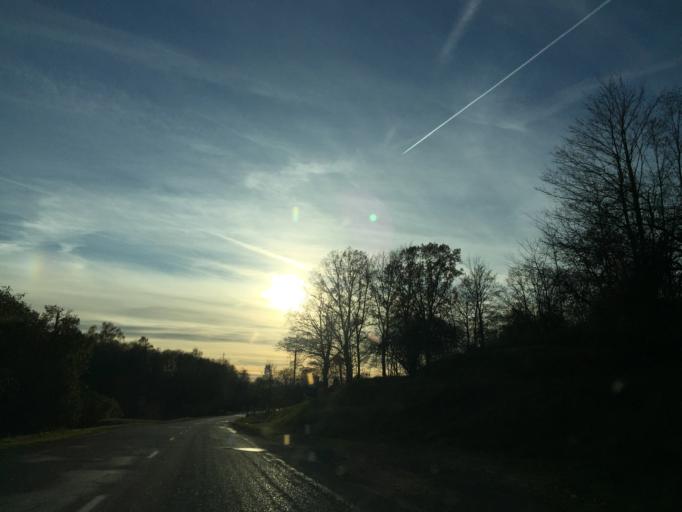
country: LV
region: Skriveri
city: Skriveri
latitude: 56.6355
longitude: 25.1073
